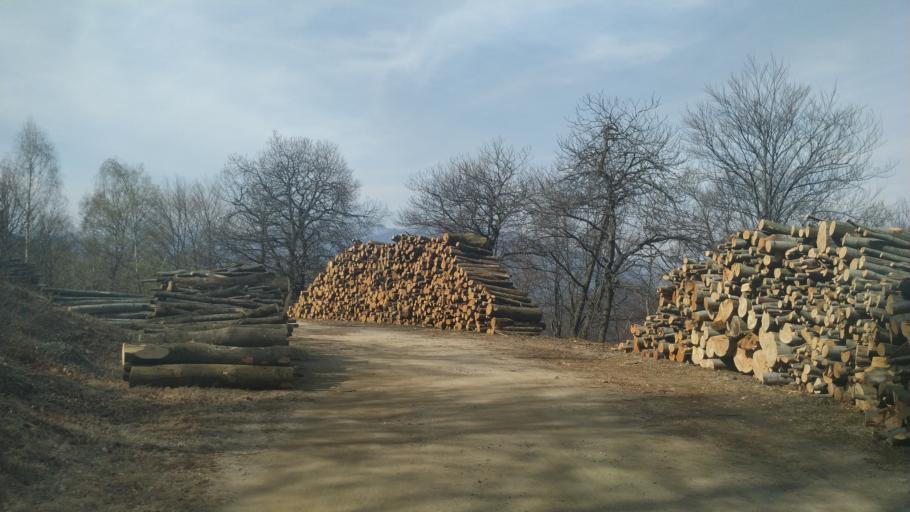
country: IT
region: Piedmont
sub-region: Provincia di Vercelli
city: Civiasco
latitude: 45.8058
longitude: 8.3142
